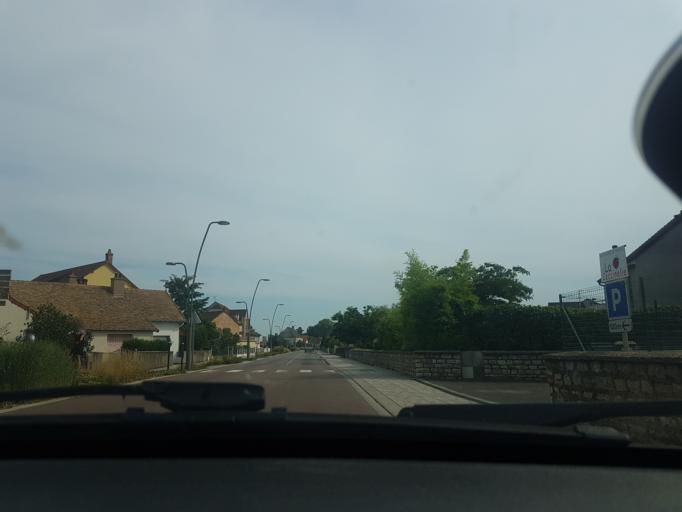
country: FR
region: Bourgogne
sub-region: Departement de Saone-et-Loire
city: Saint-Marcel
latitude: 46.7724
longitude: 4.8931
